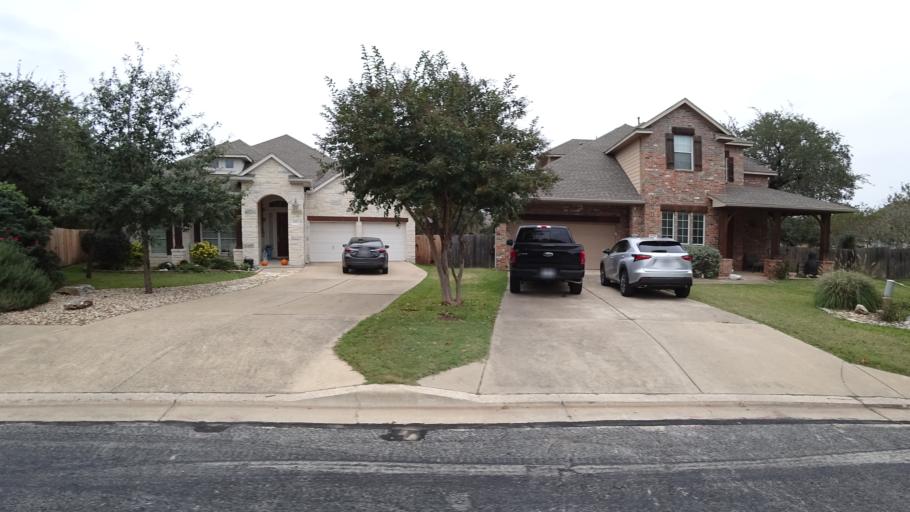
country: US
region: Texas
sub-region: Travis County
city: Shady Hollow
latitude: 30.1888
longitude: -97.8992
